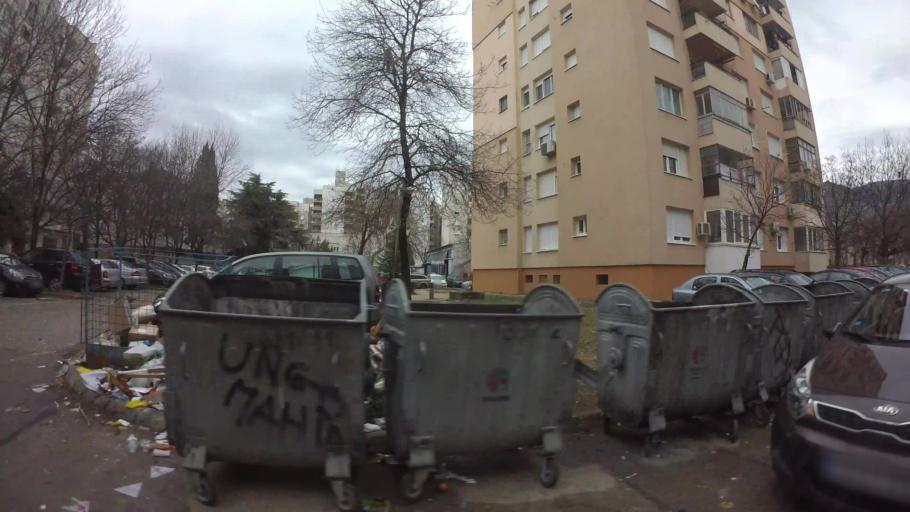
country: BA
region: Federation of Bosnia and Herzegovina
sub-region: Hercegovacko-Bosanski Kanton
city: Mostar
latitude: 43.3467
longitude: 17.8015
